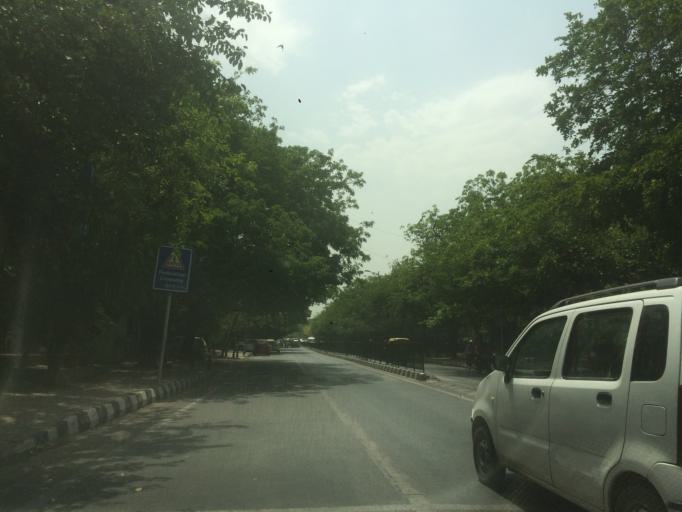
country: IN
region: NCT
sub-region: New Delhi
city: New Delhi
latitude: 28.5550
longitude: 77.2241
